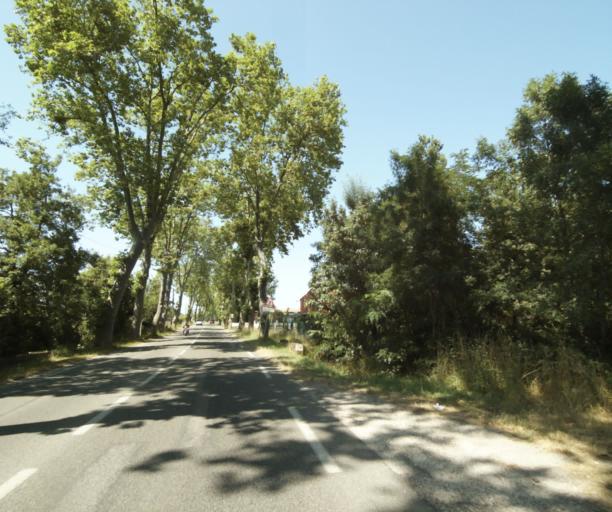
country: FR
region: Midi-Pyrenees
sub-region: Departement du Tarn-et-Garonne
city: Montauban
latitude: 44.0415
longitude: 1.3567
